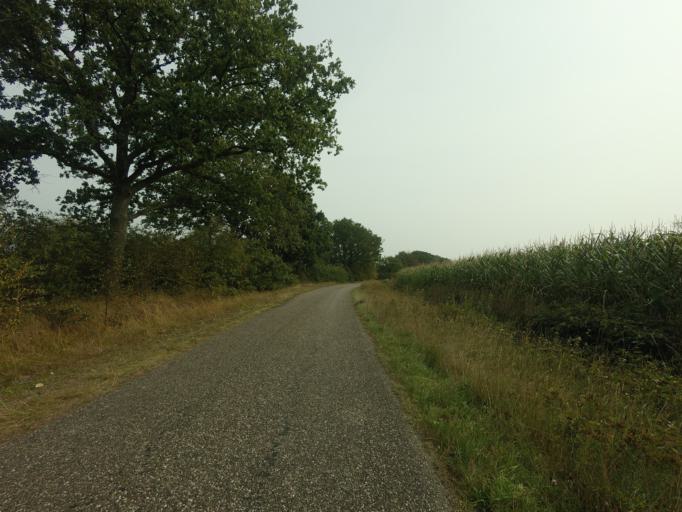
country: NL
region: Drenthe
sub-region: Gemeente Tynaarlo
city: Vries
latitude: 53.1142
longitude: 6.5415
